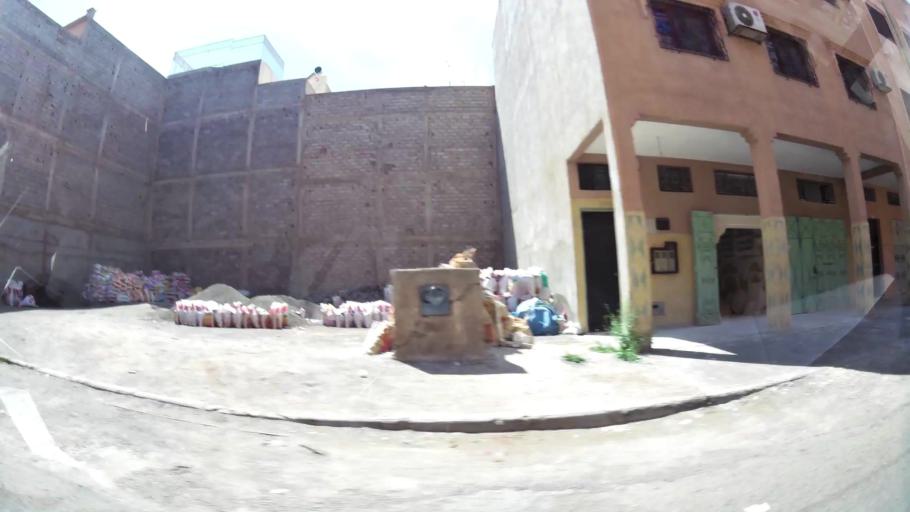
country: MA
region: Marrakech-Tensift-Al Haouz
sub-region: Marrakech
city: Marrakesh
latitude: 31.6407
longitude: -8.0631
